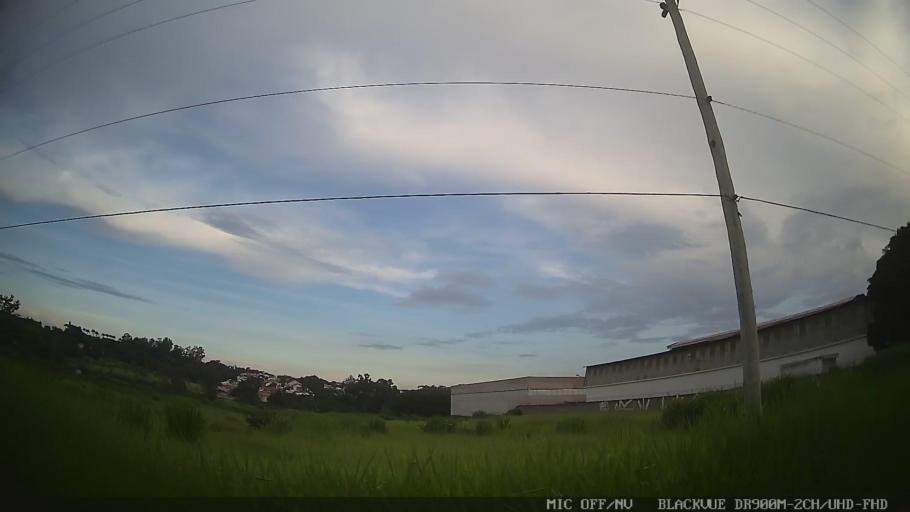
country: BR
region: Sao Paulo
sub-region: Itu
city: Itu
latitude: -23.2434
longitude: -47.3157
